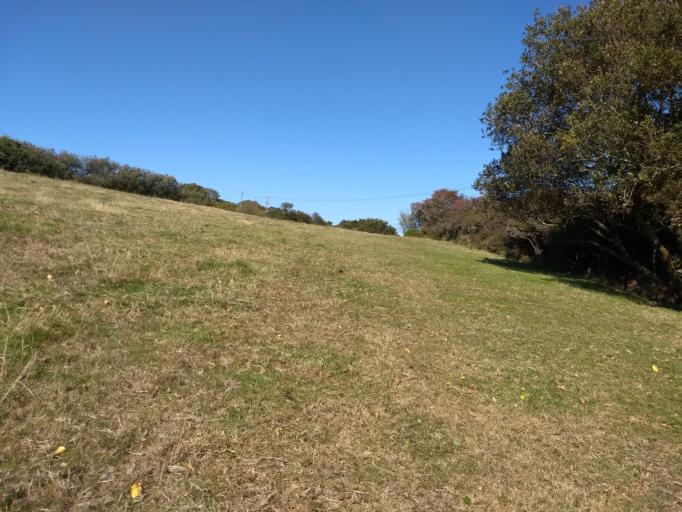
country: GB
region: England
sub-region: Isle of Wight
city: Niton
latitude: 50.6299
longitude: -1.2752
